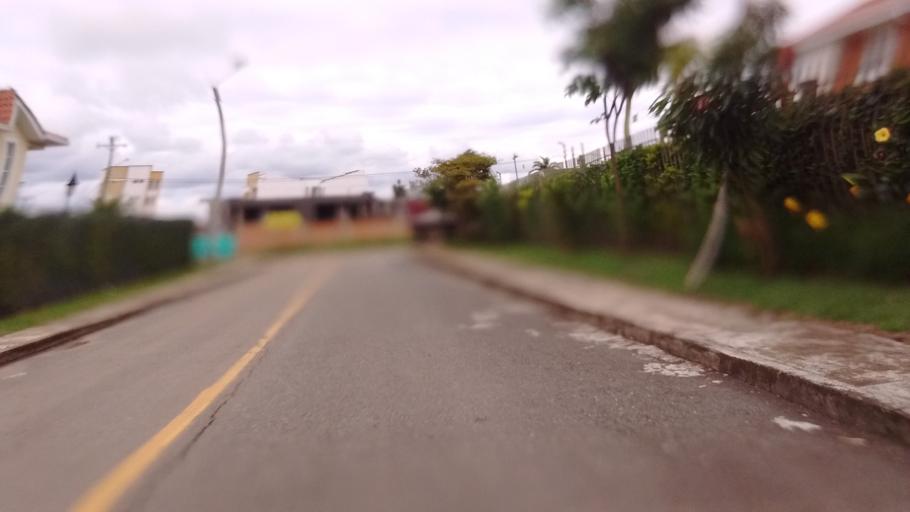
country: CO
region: Cauca
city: Popayan
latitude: 2.4794
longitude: -76.5817
